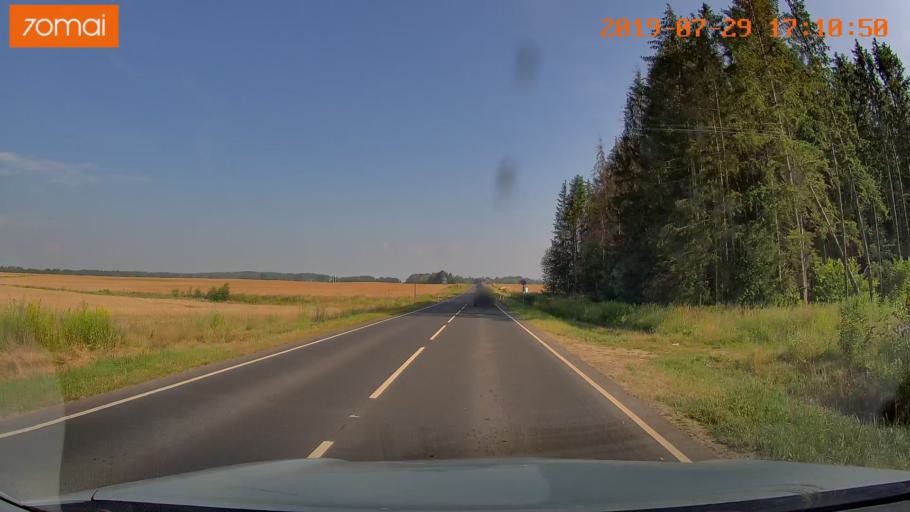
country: RU
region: Kaliningrad
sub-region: Gorod Kaliningrad
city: Kaliningrad
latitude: 54.7993
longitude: 20.3732
